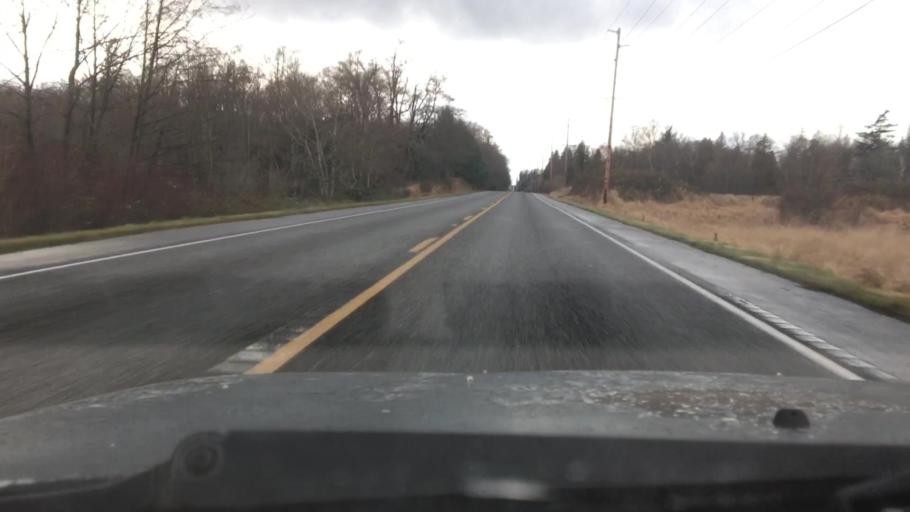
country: US
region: Washington
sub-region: Whatcom County
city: Ferndale
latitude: 48.8194
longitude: -122.6459
